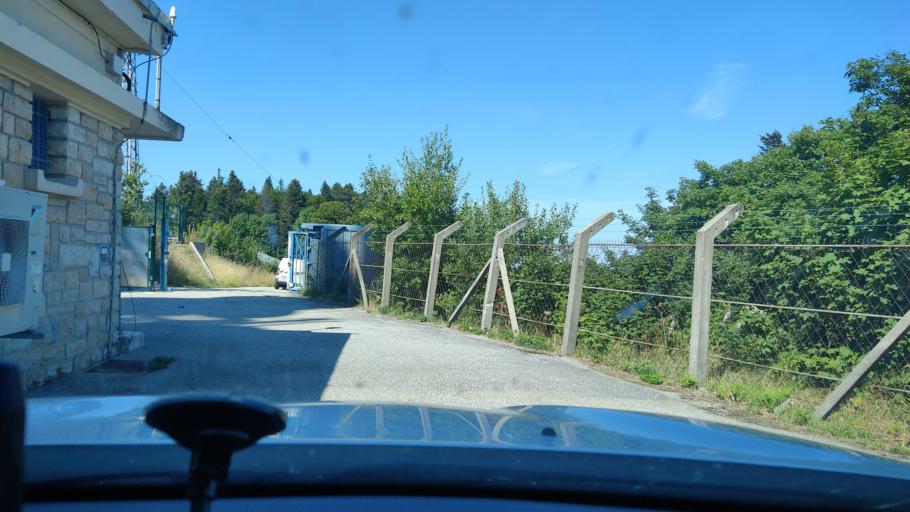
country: FR
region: Rhone-Alpes
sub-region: Departement de la Savoie
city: Le Bourget-du-Lac
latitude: 45.6599
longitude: 5.8216
